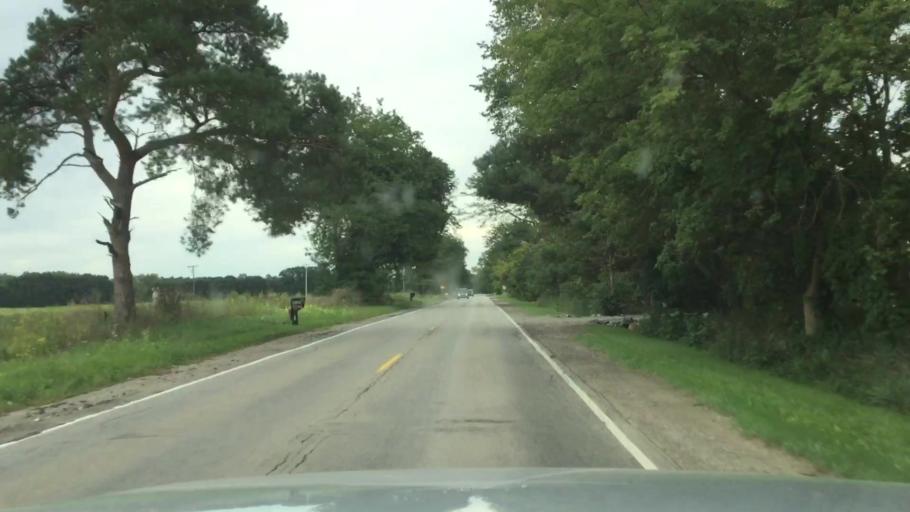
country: US
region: Michigan
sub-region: Genesee County
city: Argentine
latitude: 42.8034
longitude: -83.8731
